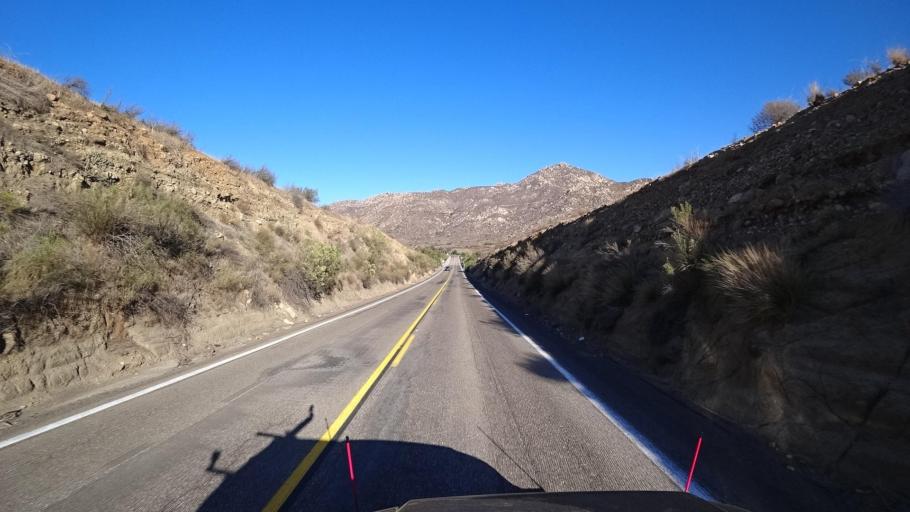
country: MX
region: Baja California
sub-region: Tecate
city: Lomas de Santa Anita
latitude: 32.6067
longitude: -116.6985
